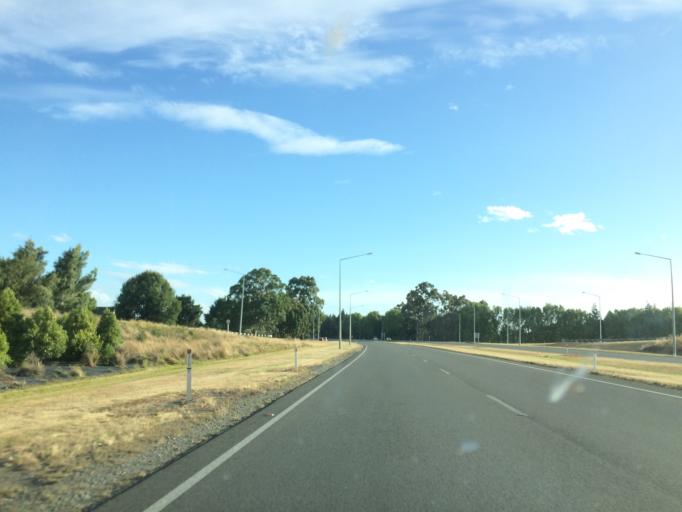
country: NZ
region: Canterbury
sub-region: Waimakariri District
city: Kaiapoi
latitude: -43.3869
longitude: 172.6411
